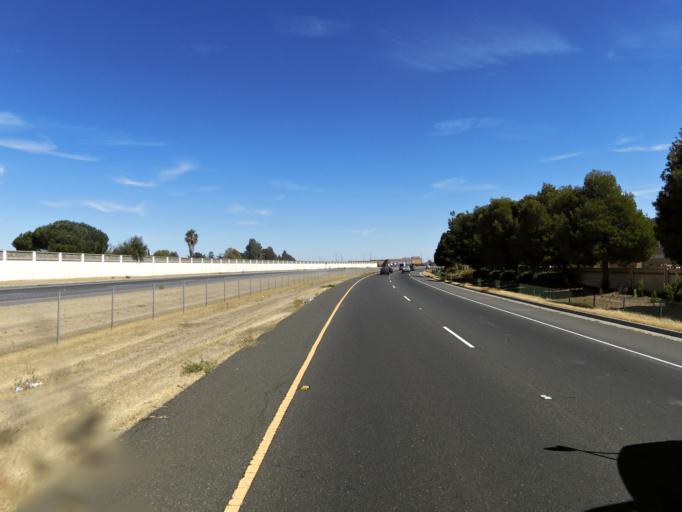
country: US
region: California
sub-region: Solano County
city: Fairfield
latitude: 38.2432
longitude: -121.9976
